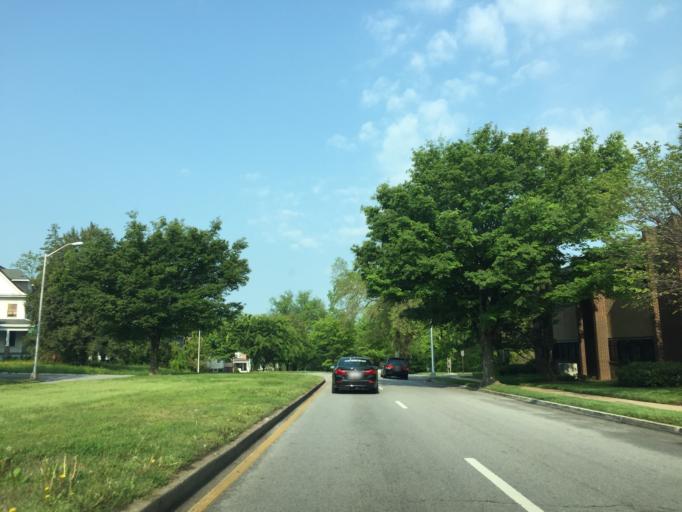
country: US
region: Maryland
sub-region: Baltimore County
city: Woodlawn
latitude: 39.3142
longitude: -76.6771
